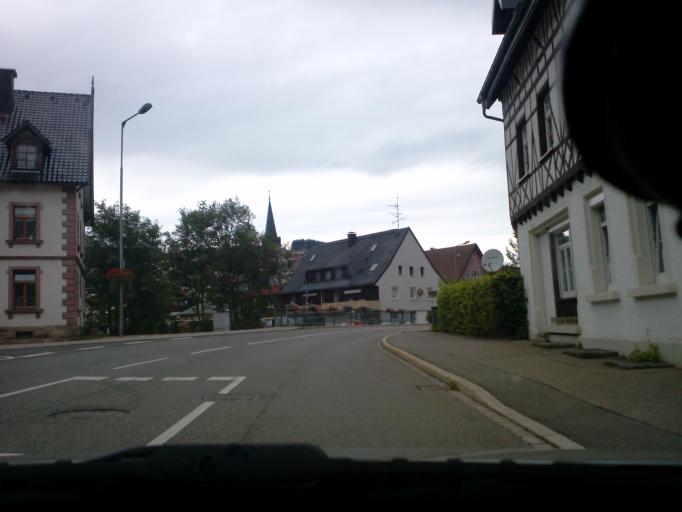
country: DE
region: Baden-Wuerttemberg
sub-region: Freiburg Region
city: Vohrenbach
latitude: 48.0434
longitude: 8.3066
